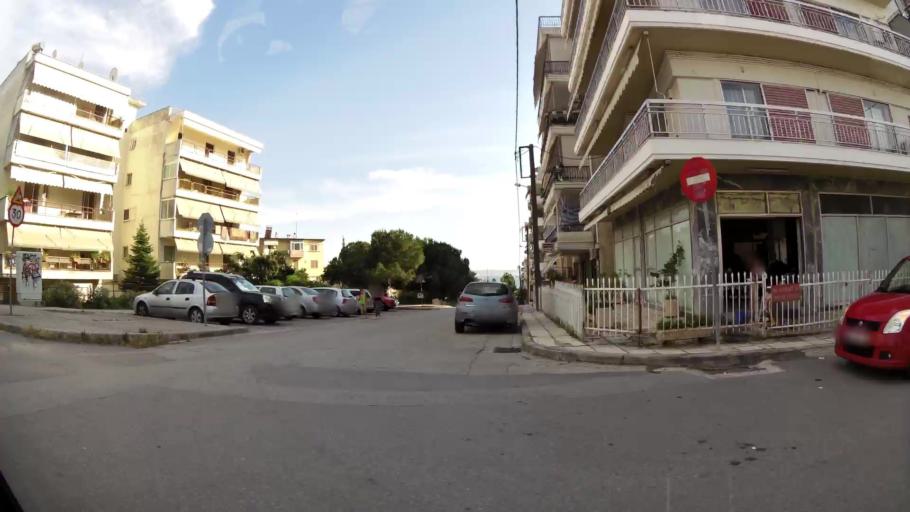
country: GR
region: Central Macedonia
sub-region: Nomos Thessalonikis
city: Kalamaria
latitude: 40.5694
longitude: 22.9620
